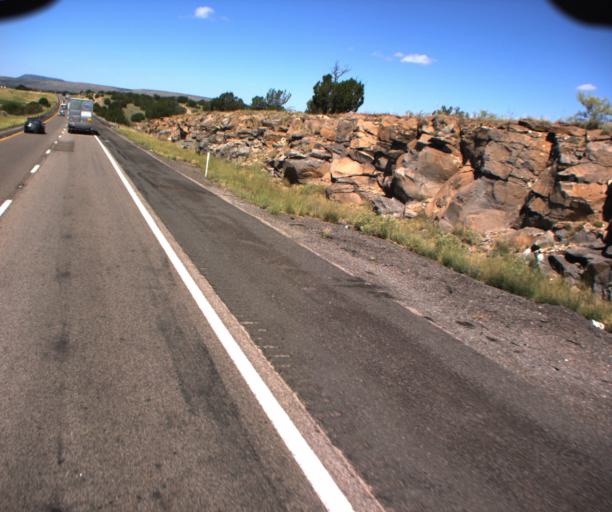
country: US
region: Arizona
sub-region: Mohave County
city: Peach Springs
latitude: 35.3231
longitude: -112.9202
